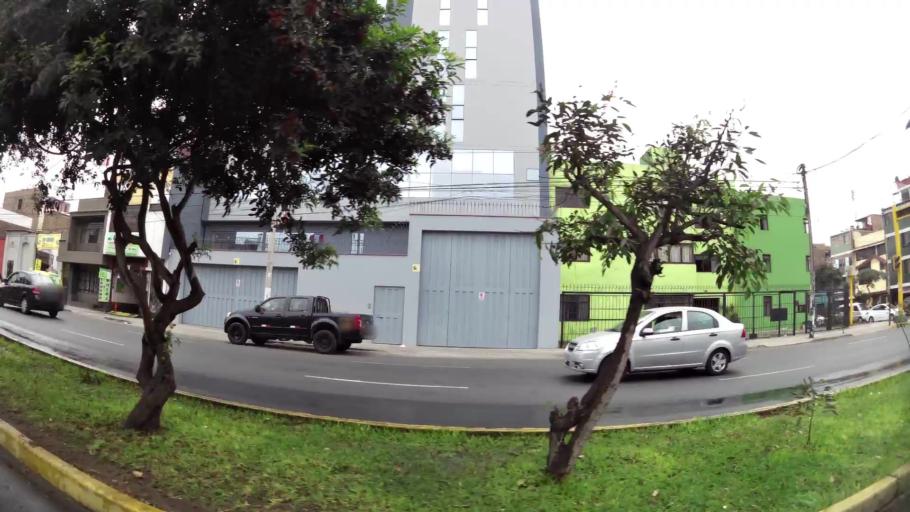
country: PE
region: Lima
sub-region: Lima
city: San Luis
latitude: -12.0809
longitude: -77.0284
